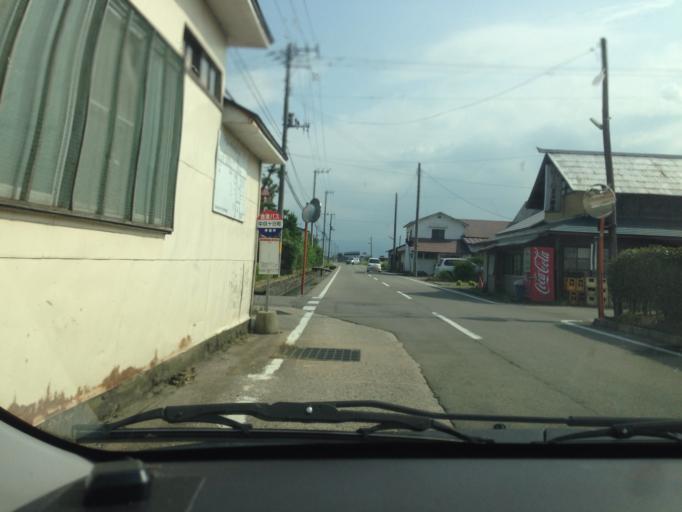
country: JP
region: Fukushima
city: Kitakata
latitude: 37.5673
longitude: 139.8533
